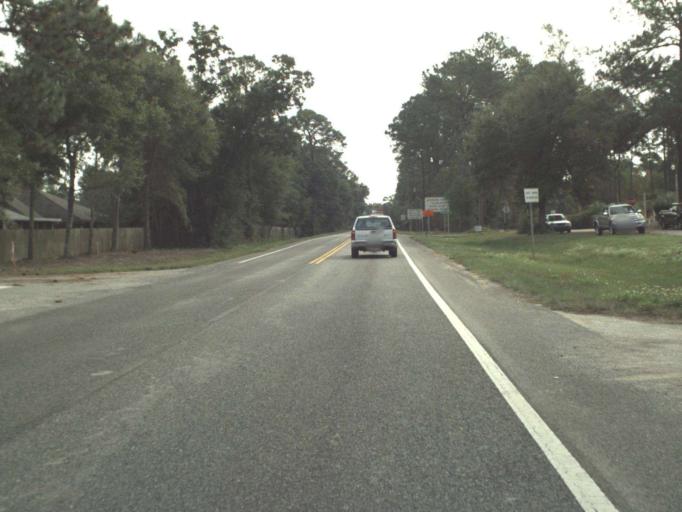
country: US
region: Florida
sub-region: Escambia County
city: Myrtle Grove
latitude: 30.4011
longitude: -87.4242
